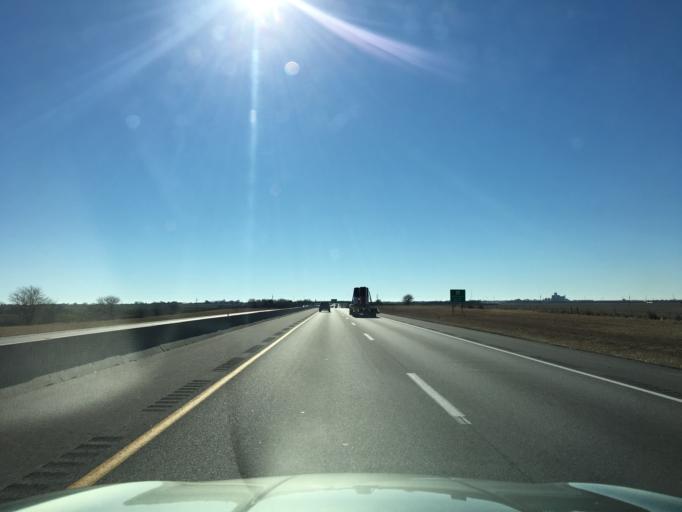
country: US
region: Kansas
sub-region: Sumner County
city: Wellington
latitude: 37.2958
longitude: -97.3403
